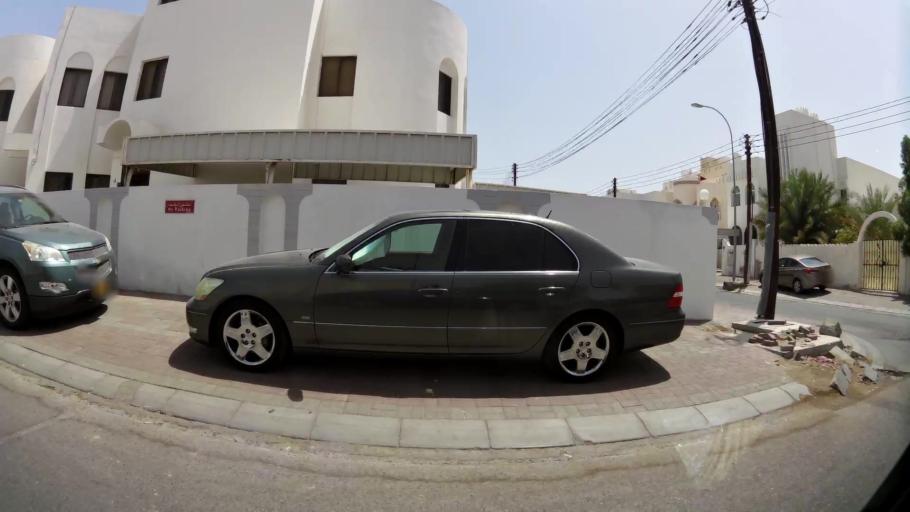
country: OM
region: Muhafazat Masqat
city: Bawshar
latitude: 23.5897
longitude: 58.4329
